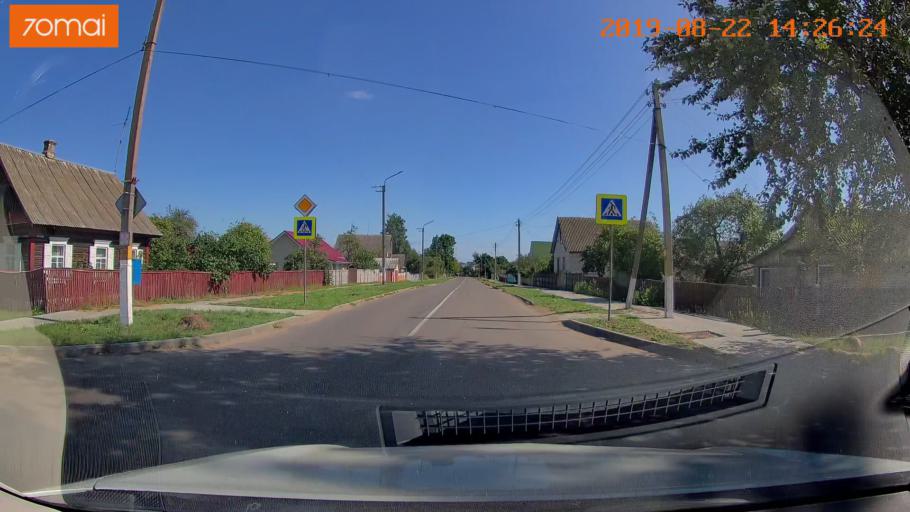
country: BY
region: Mogilev
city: Asipovichy
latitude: 53.2993
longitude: 28.6153
